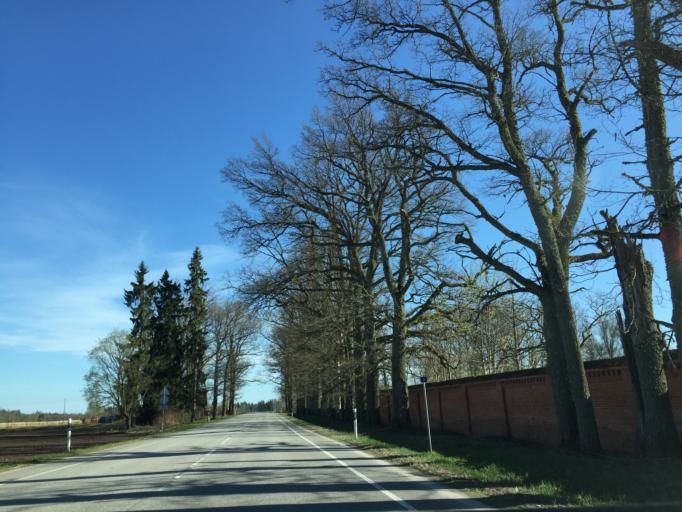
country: EE
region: Vorumaa
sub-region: Antsla vald
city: Vana-Antsla
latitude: 57.9026
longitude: 26.2863
